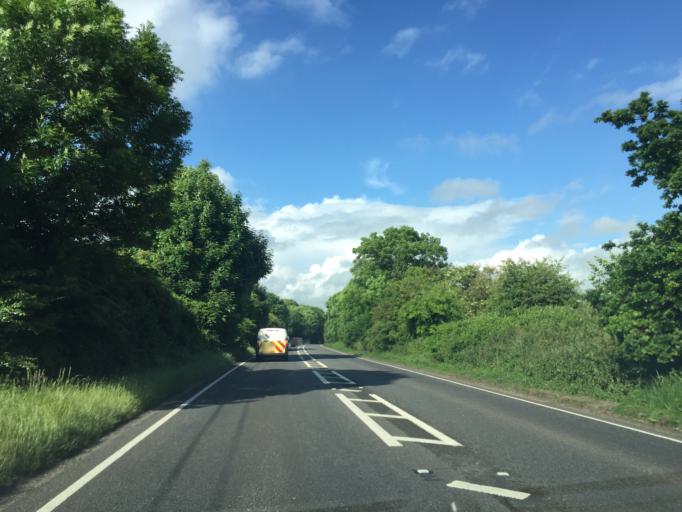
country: GB
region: England
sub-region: Dorset
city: Dorchester
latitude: 50.7291
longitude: -2.4055
